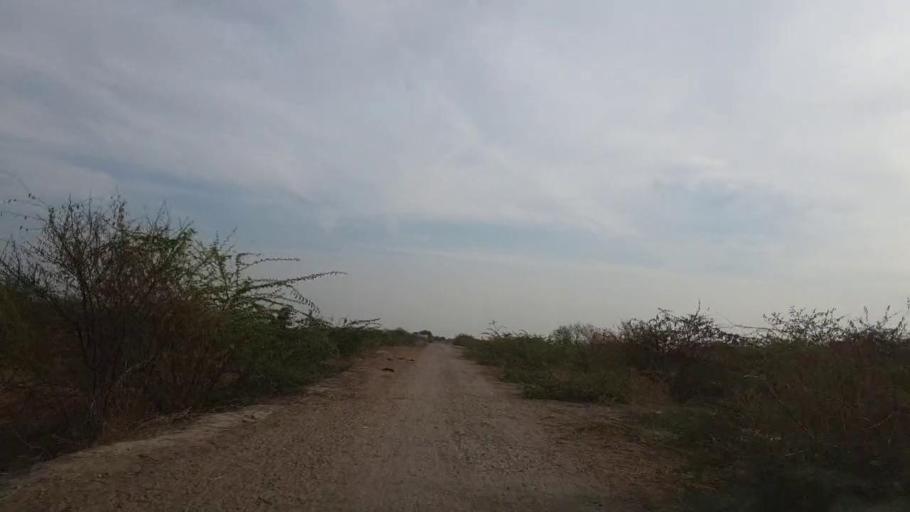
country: PK
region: Sindh
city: Nabisar
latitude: 24.9952
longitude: 69.5182
